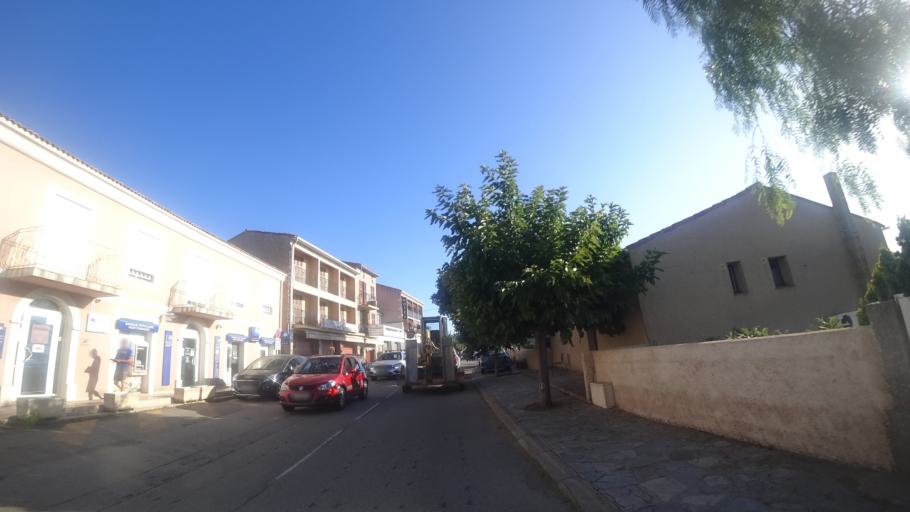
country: FR
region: Corsica
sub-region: Departement de la Corse-du-Sud
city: Cargese
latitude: 42.1371
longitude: 8.5967
